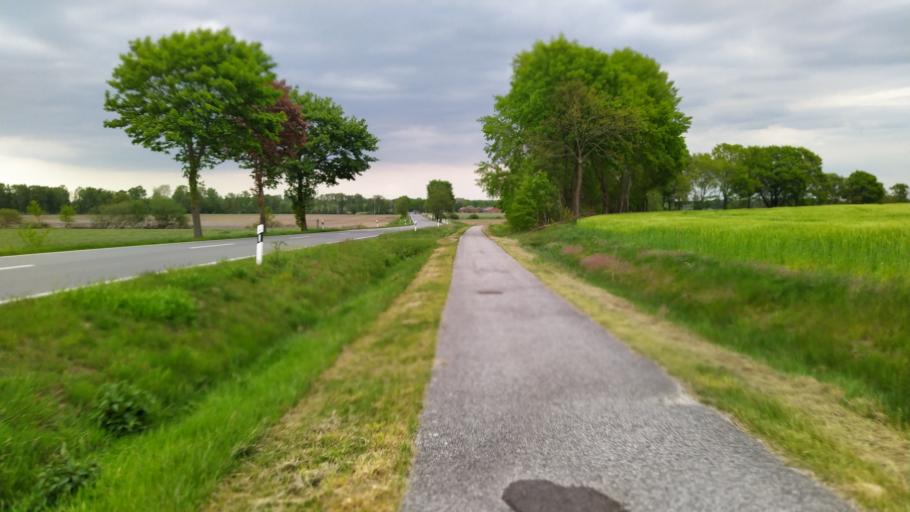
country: DE
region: Lower Saxony
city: Kirchtimke
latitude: 53.2637
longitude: 9.1892
